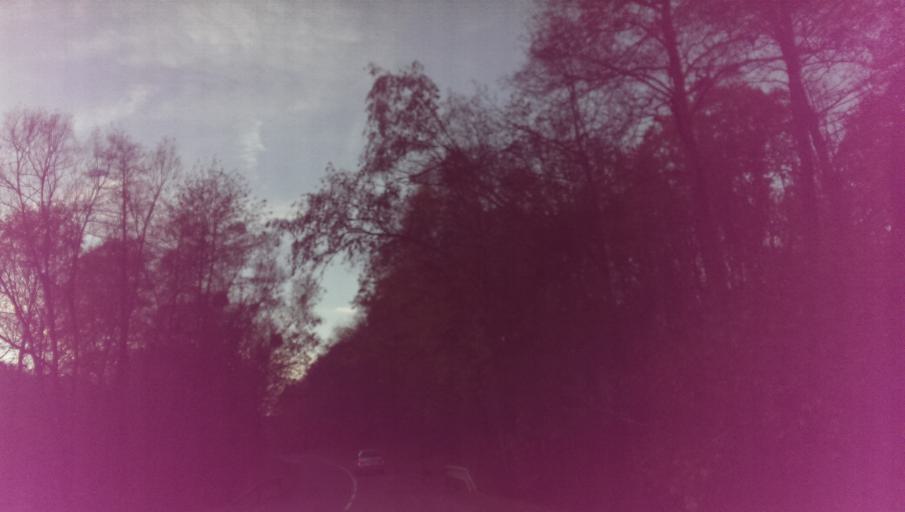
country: CZ
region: Zlin
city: Tecovice
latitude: 49.1925
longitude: 17.6074
